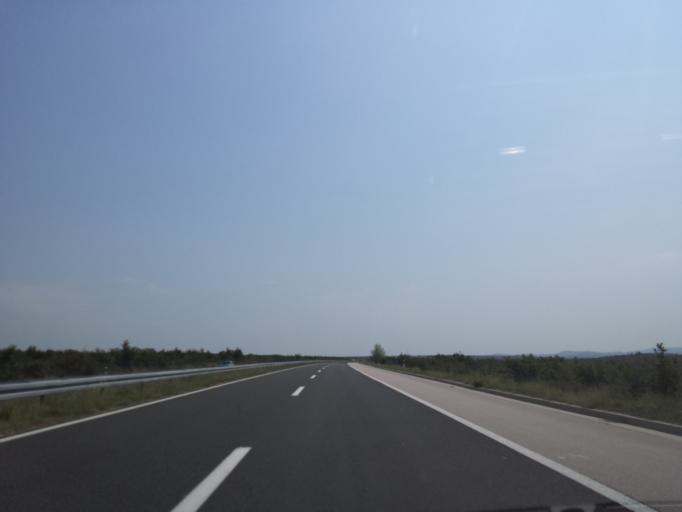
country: HR
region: Zadarska
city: Polaca
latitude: 44.0387
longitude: 15.5566
